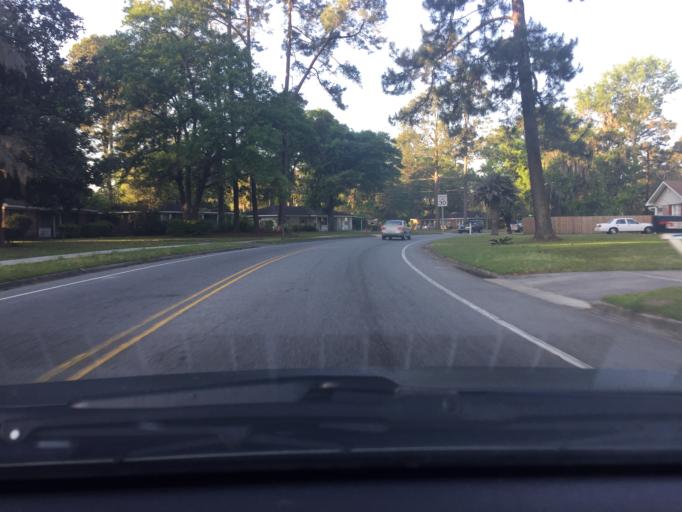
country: US
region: Georgia
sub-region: Chatham County
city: Montgomery
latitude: 31.9872
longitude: -81.1457
